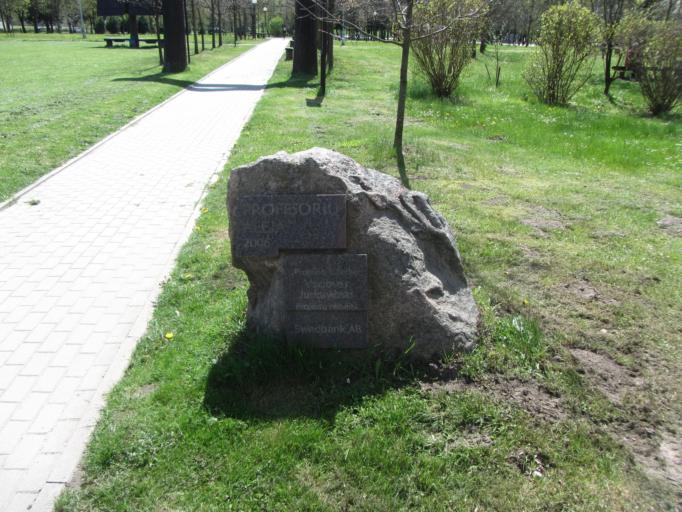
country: LT
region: Vilnius County
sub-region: Vilnius
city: Fabijoniskes
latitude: 54.7514
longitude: 25.2786
